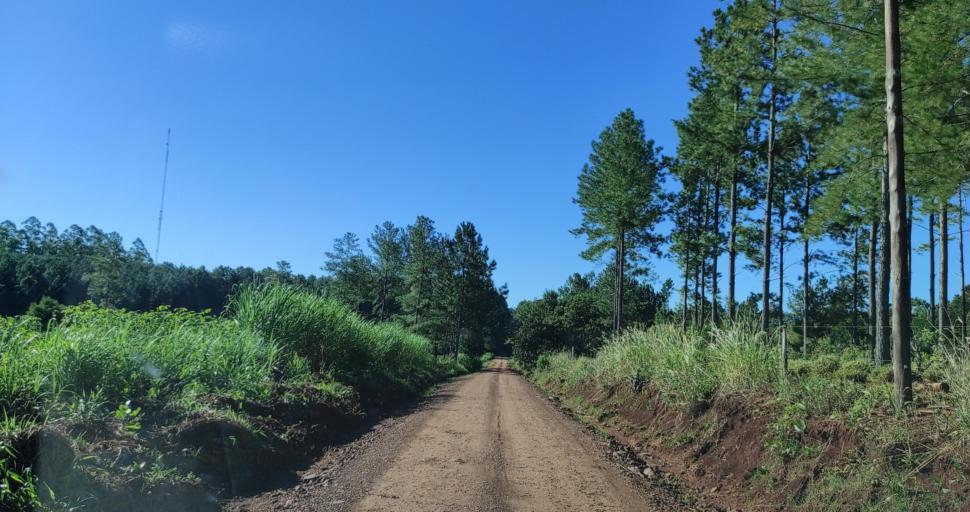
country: AR
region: Misiones
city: Capiovi
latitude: -26.9235
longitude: -55.0005
